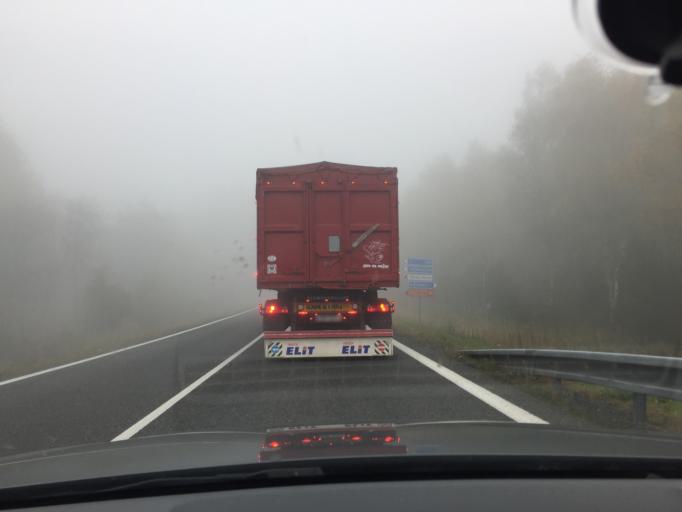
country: CZ
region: Ustecky
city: Libouchec
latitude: 50.7678
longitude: 13.9719
